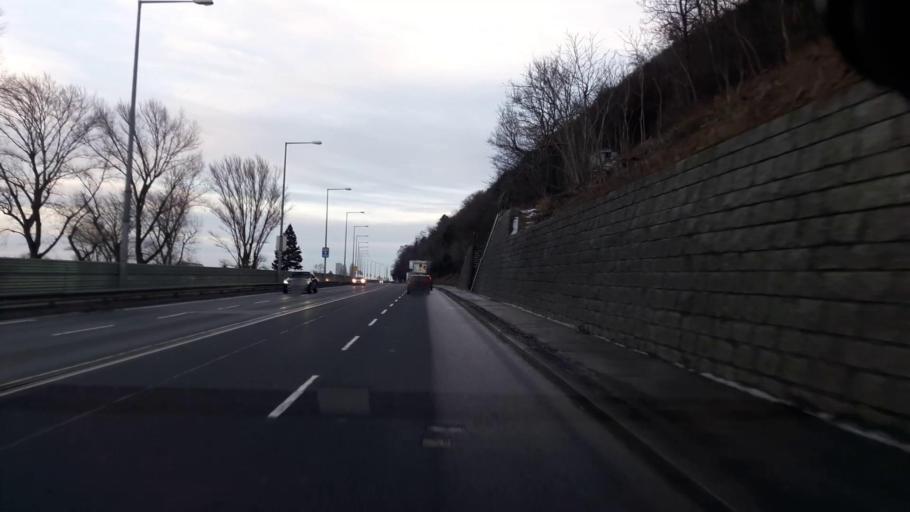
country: AT
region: Lower Austria
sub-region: Politischer Bezirk Korneuburg
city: Langenzersdorf
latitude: 48.2822
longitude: 16.3487
